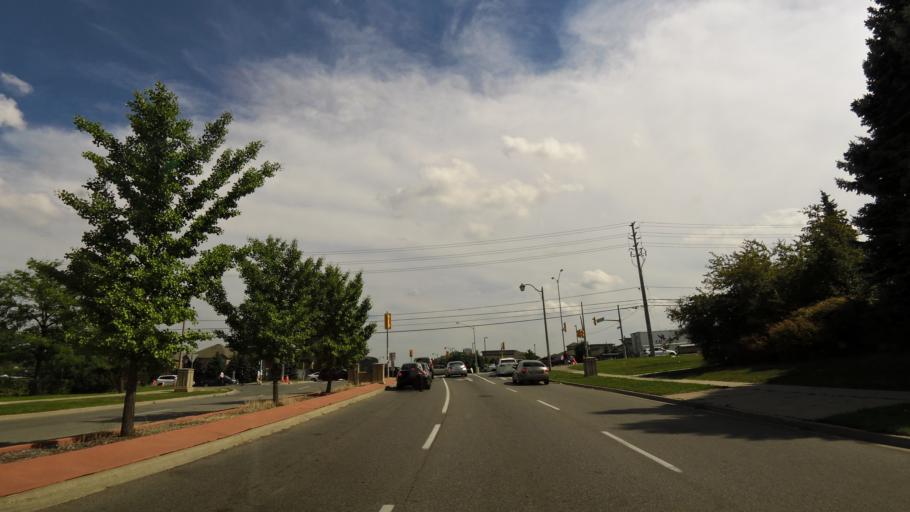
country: CA
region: Ontario
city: Brampton
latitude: 43.7583
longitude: -79.7308
